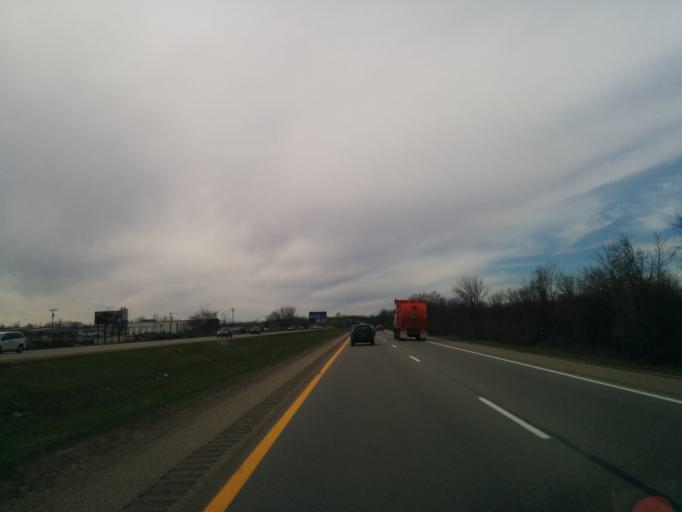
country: US
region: Michigan
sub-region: Kent County
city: Grandville
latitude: 42.9243
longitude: -85.7514
